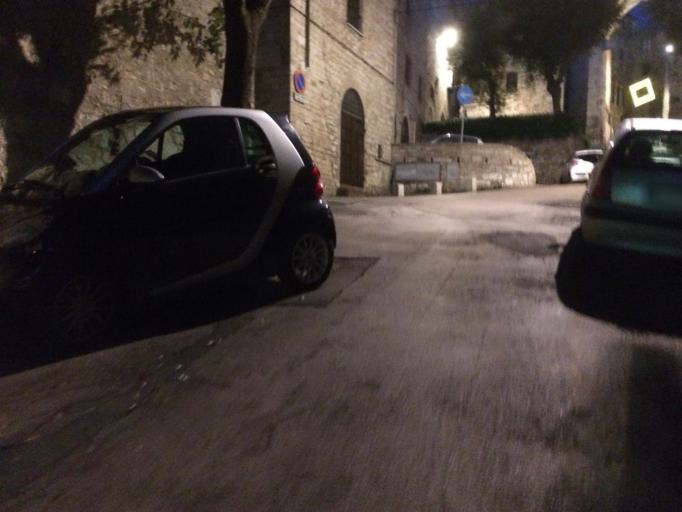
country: IT
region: Umbria
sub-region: Provincia di Perugia
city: Perugia
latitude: 43.1130
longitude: 12.3834
